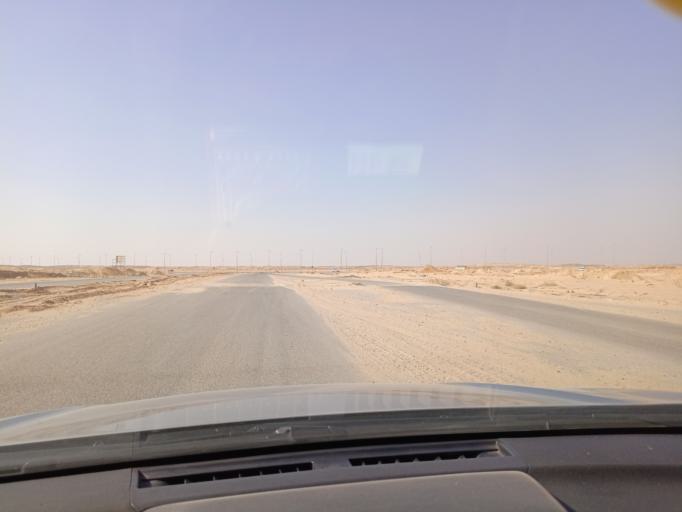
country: EG
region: Muhafazat al Qalyubiyah
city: Al Khankah
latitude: 30.0418
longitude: 31.7143
